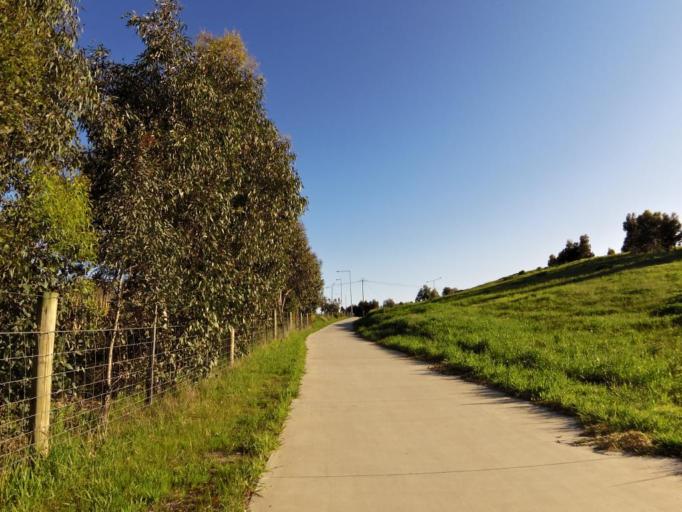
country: AU
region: Victoria
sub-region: Monash
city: Mulgrave
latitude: -37.9239
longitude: 145.2129
